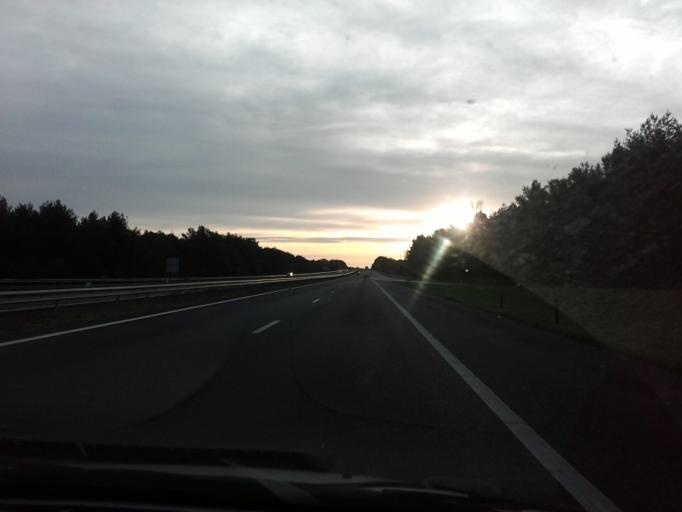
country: NL
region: North Brabant
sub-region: Gemeente Cranendonck
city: Cranendonck
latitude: 51.2955
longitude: 5.6320
